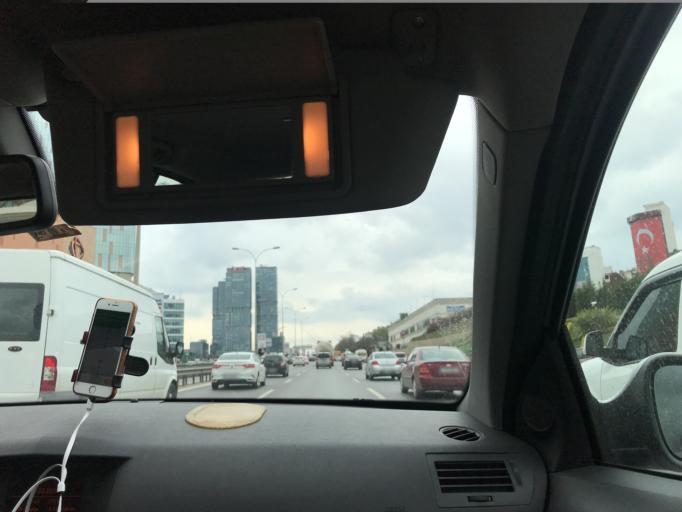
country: TR
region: Istanbul
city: Maltepe
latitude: 40.9204
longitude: 29.1688
